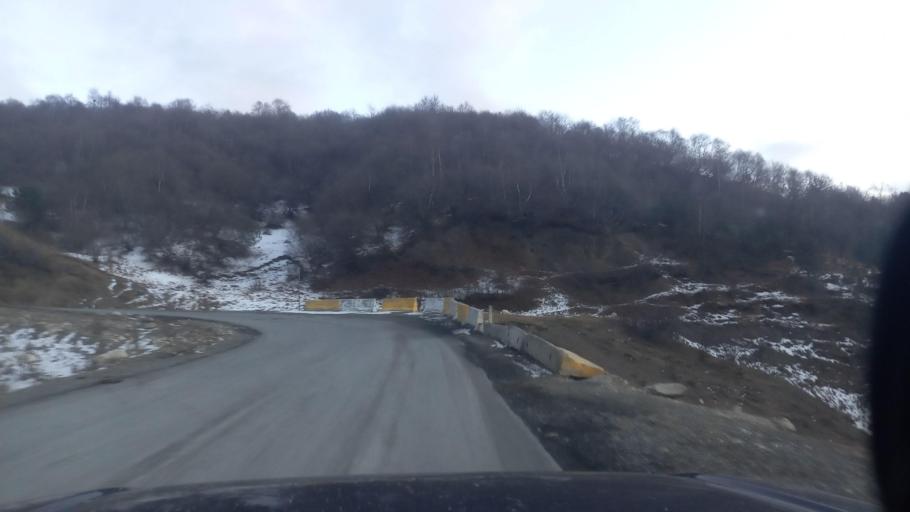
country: RU
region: Ingushetiya
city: Dzhayrakh
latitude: 42.8214
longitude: 44.8176
